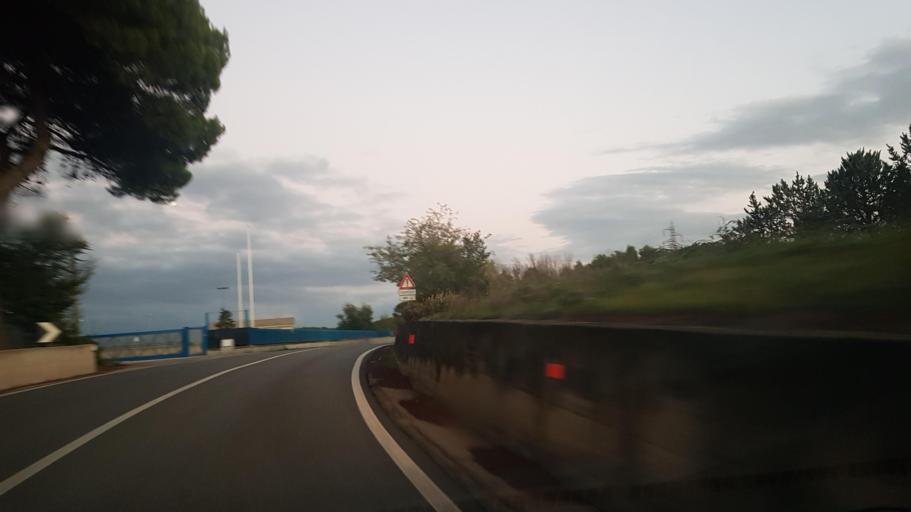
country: IT
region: Basilicate
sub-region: Provincia di Matera
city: Matera
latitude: 40.6782
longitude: 16.6568
